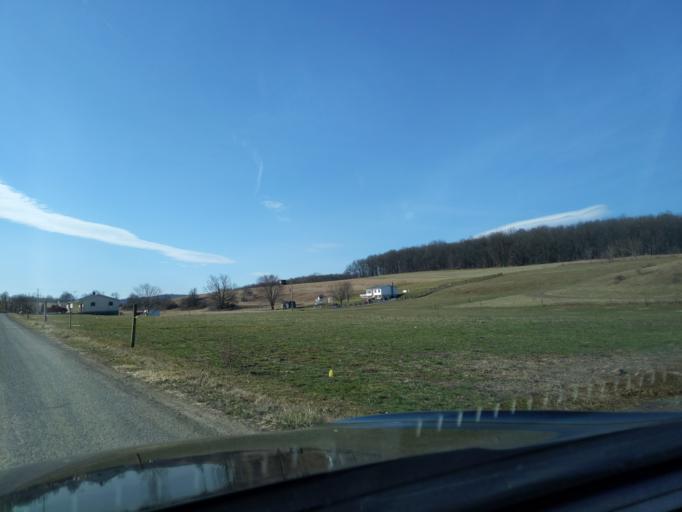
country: US
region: Pennsylvania
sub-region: Blair County
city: Martinsburg
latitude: 40.3879
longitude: -78.2750
